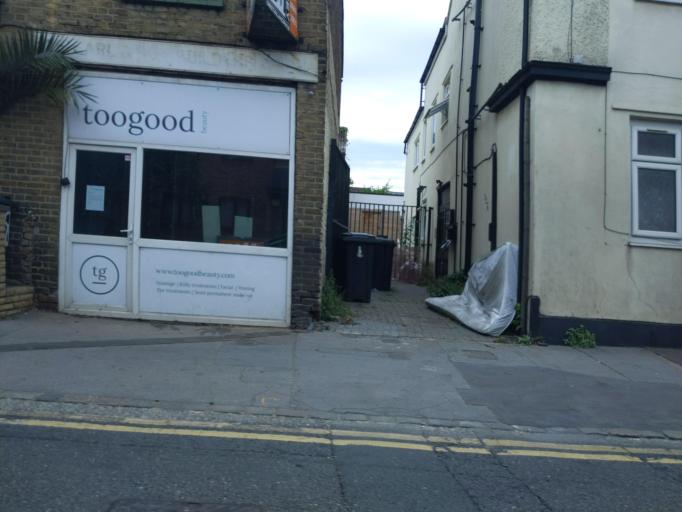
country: GB
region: England
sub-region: Greater London
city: South Croydon
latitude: 51.3656
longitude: -0.0999
